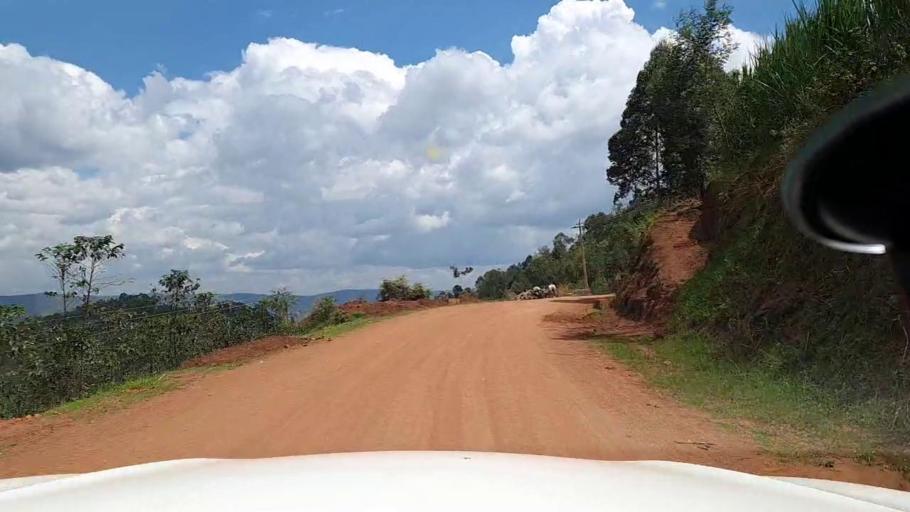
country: RW
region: Kigali
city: Kigali
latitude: -1.7836
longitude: 29.8422
